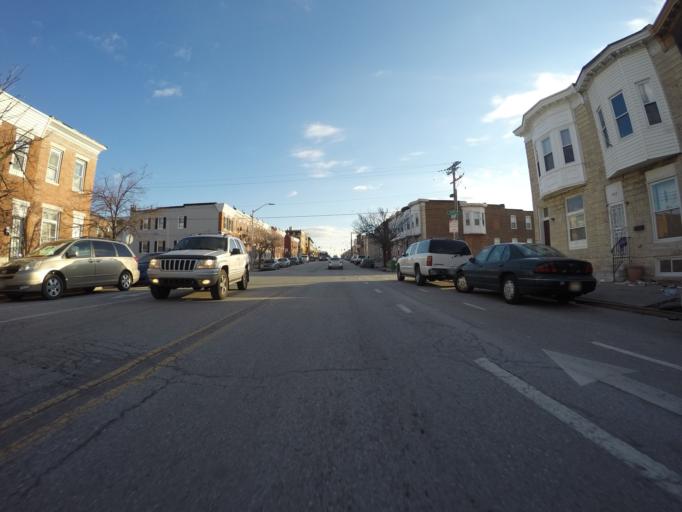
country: US
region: Maryland
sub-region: City of Baltimore
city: Baltimore
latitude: 39.2941
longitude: -76.5695
